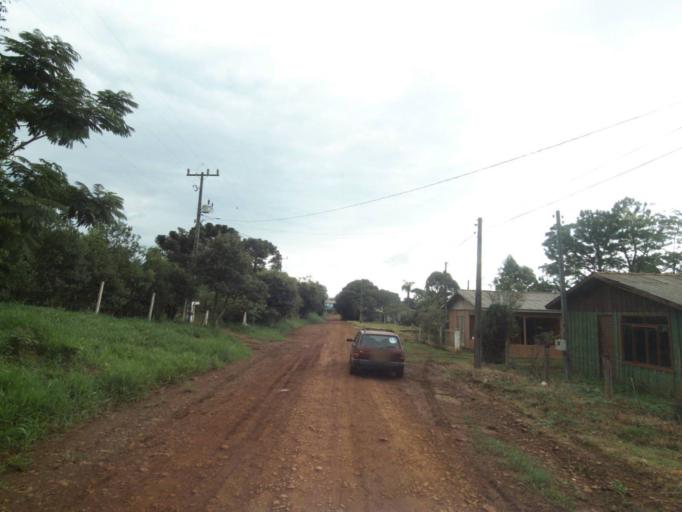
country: BR
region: Parana
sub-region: Pitanga
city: Pitanga
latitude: -24.8975
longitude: -51.9623
